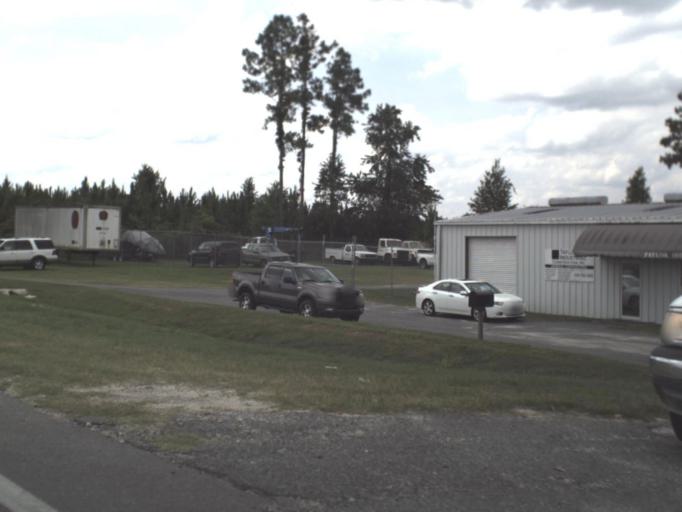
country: US
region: Florida
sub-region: Hamilton County
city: Jasper
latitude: 30.5029
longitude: -82.9409
